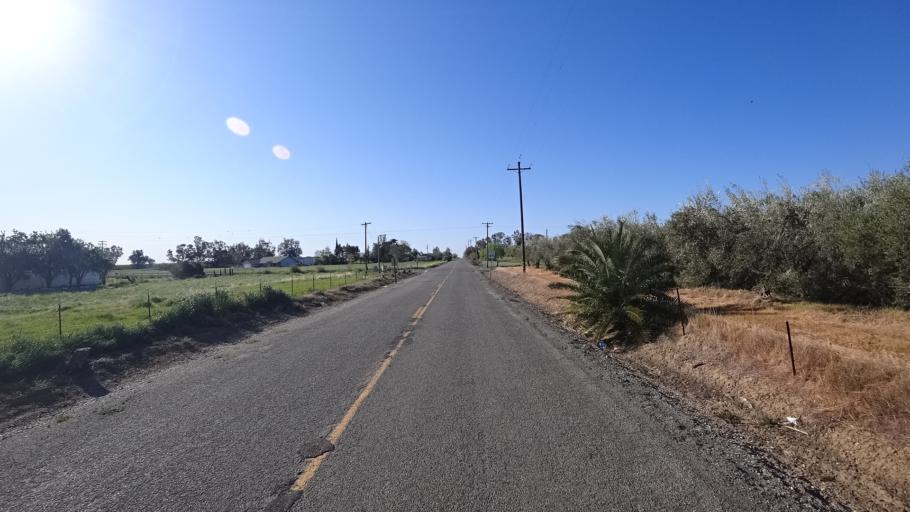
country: US
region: California
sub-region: Glenn County
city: Orland
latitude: 39.7976
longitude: -122.1040
